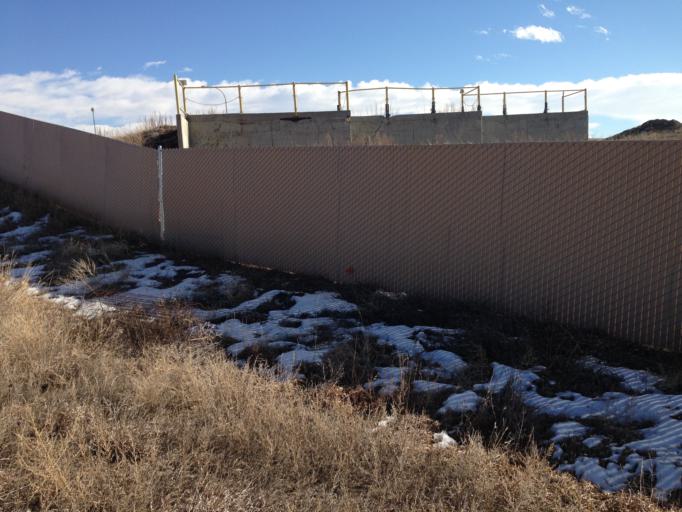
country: US
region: Colorado
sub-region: Boulder County
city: Erie
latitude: 40.0293
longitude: -105.0244
